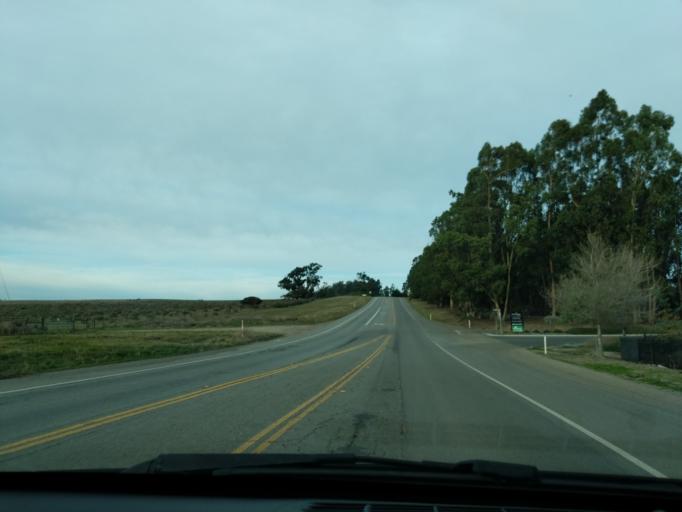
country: US
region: California
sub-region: San Luis Obispo County
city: Callender
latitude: 35.0224
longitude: -120.5628
